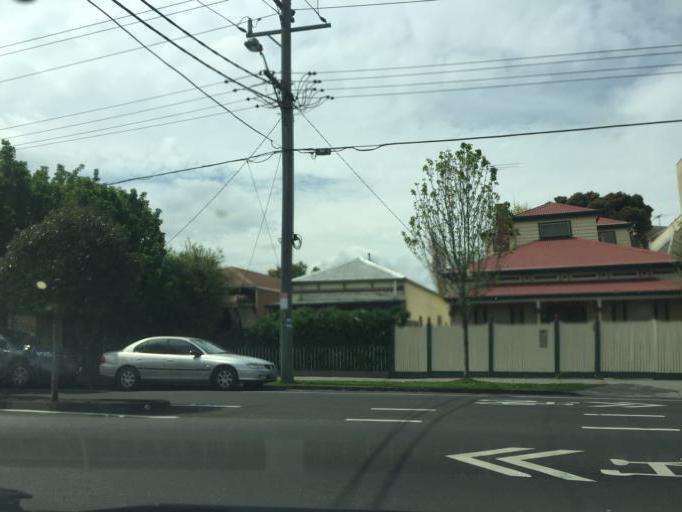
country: AU
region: Victoria
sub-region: Maribyrnong
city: Seddon
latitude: -37.8091
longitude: 144.8899
